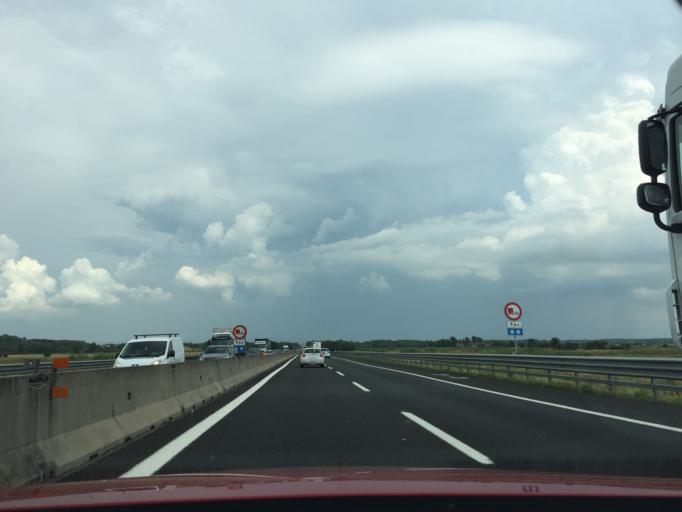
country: IT
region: Tuscany
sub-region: Provincia di Lucca
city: Porcari
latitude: 43.8188
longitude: 10.6297
